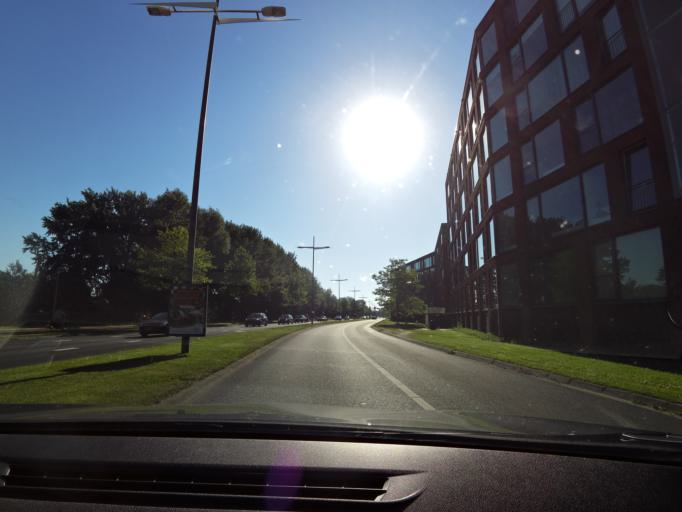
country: NL
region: Overijssel
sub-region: Gemeente Deventer
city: Deventer
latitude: 52.2536
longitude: 6.1714
